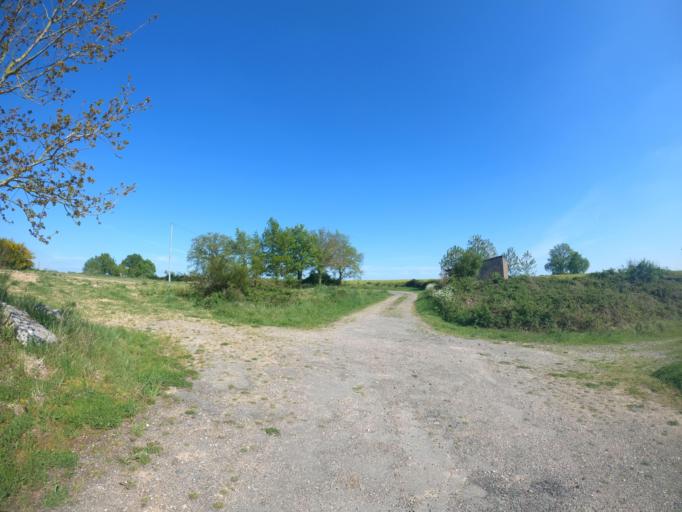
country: FR
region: Poitou-Charentes
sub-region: Departement des Deux-Sevres
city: Moncoutant
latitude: 46.6801
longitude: -0.5347
